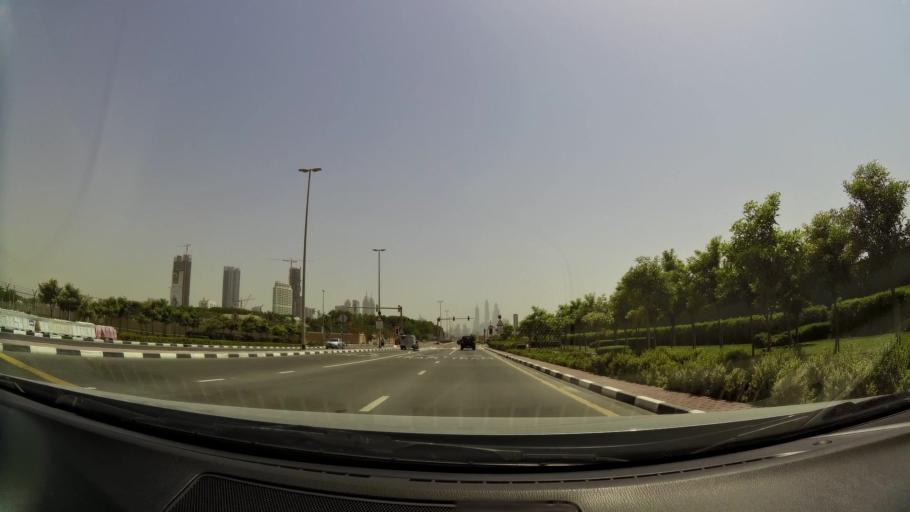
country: AE
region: Dubai
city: Dubai
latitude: 25.1196
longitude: 55.1811
